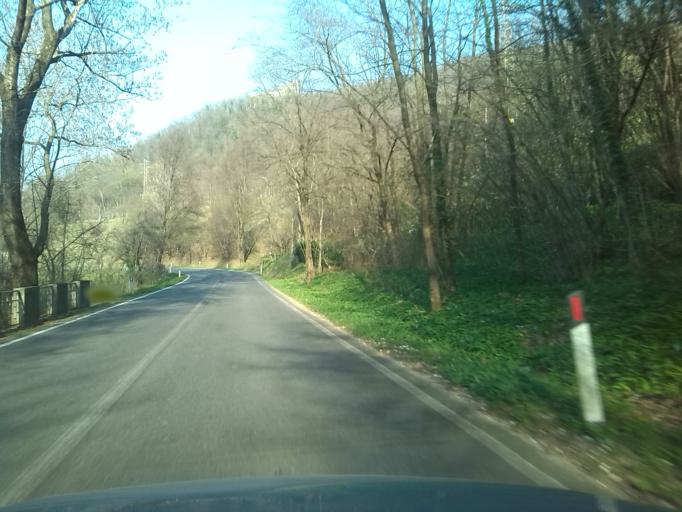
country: IT
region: Friuli Venezia Giulia
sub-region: Provincia di Udine
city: San Pietro al Natisone
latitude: 46.1056
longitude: 13.4729
